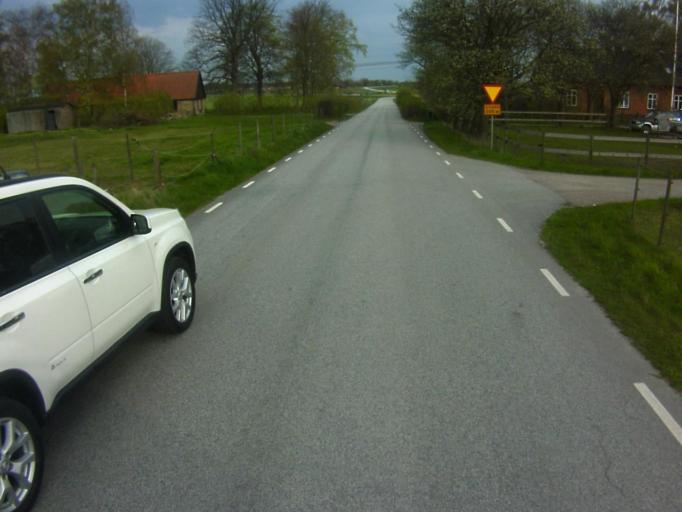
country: SE
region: Skane
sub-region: Kavlinge Kommun
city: Hofterup
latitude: 55.7639
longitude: 12.9774
